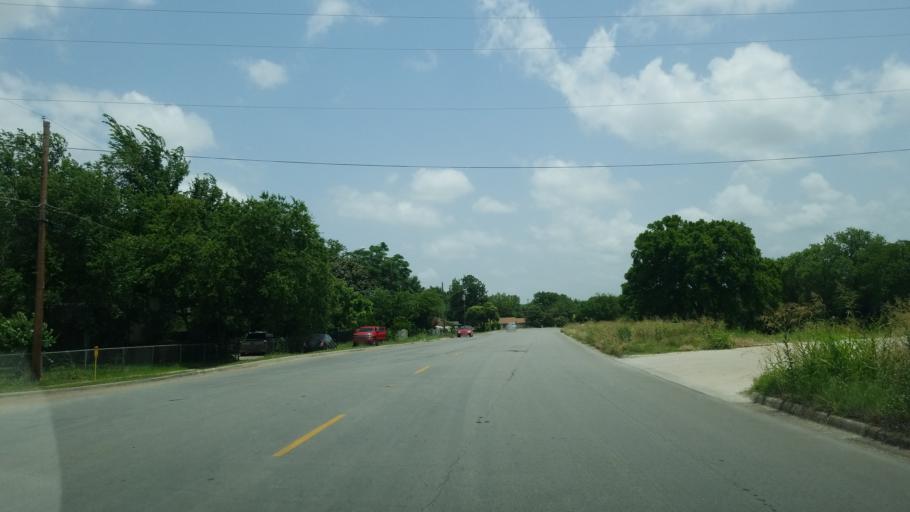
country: US
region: Texas
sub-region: Dallas County
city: Cockrell Hill
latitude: 32.7915
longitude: -96.8857
